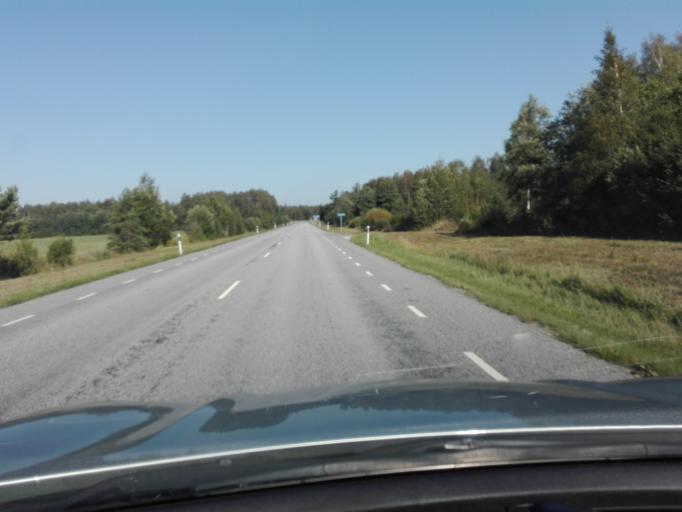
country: EE
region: Raplamaa
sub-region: Rapla vald
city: Rapla
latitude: 59.0148
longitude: 24.7762
